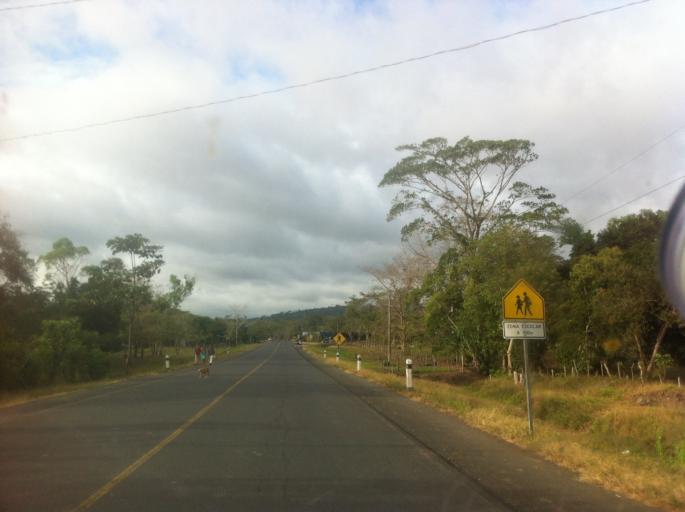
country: NI
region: Rio San Juan
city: San Carlos
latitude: 11.2378
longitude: -84.6905
